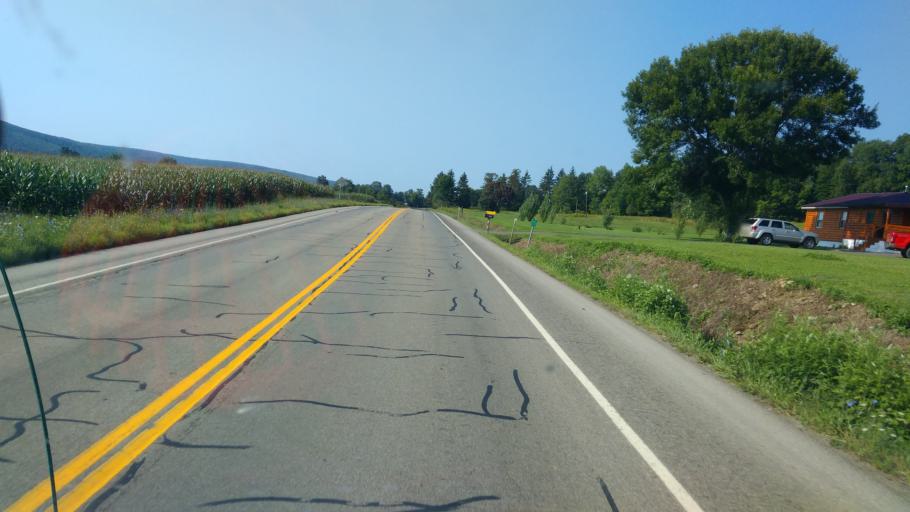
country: US
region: New York
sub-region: Allegany County
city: Friendship
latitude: 42.2992
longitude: -78.1895
